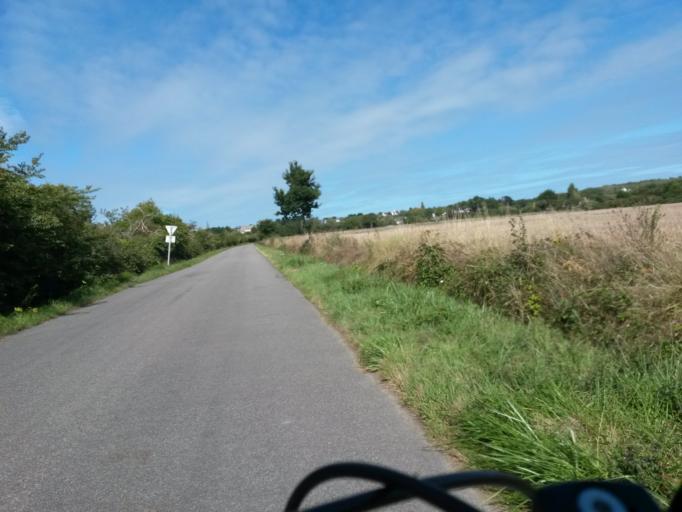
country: FR
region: Pays de la Loire
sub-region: Departement de la Loire-Atlantique
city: Guerande
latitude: 47.3139
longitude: -2.4376
